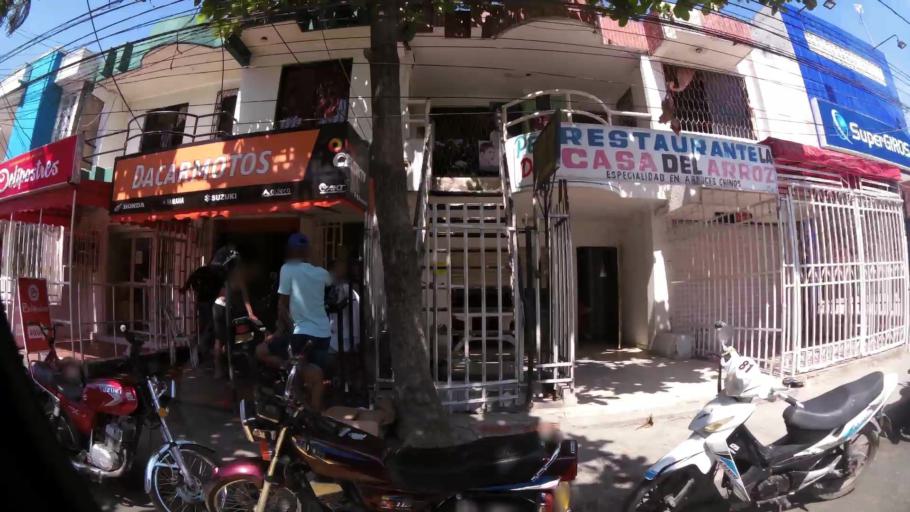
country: CO
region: Bolivar
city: Cartagena
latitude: 10.3849
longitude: -75.4608
